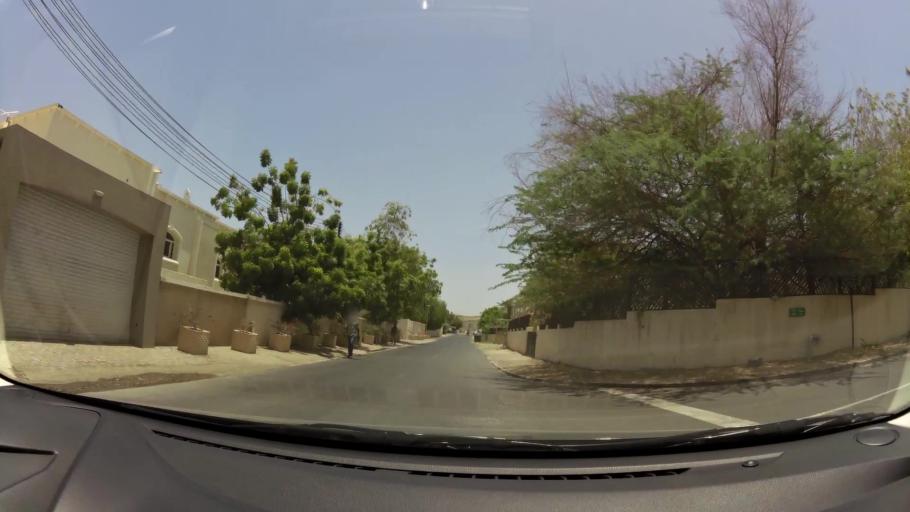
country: OM
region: Muhafazat Masqat
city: Bawshar
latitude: 23.6030
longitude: 58.4586
